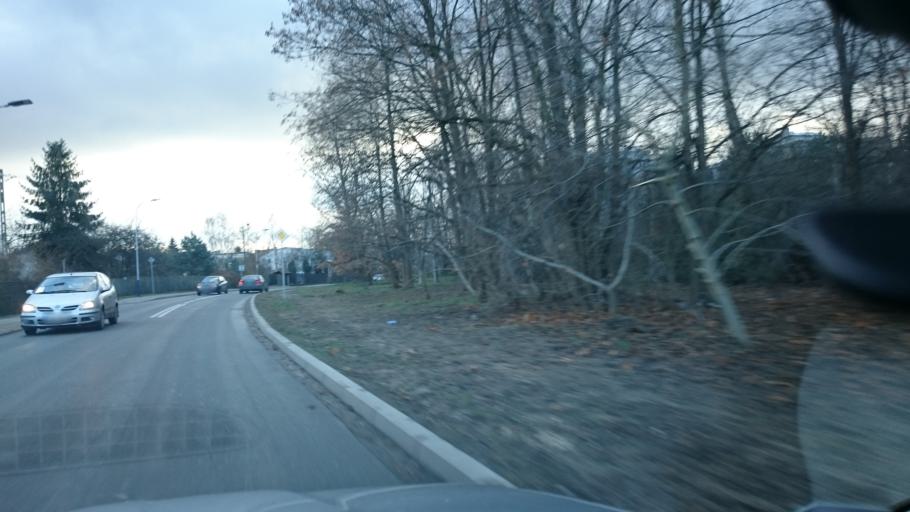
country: PL
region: Lesser Poland Voivodeship
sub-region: Powiat wielicki
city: Czarnochowice
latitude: 50.0137
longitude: 20.0281
